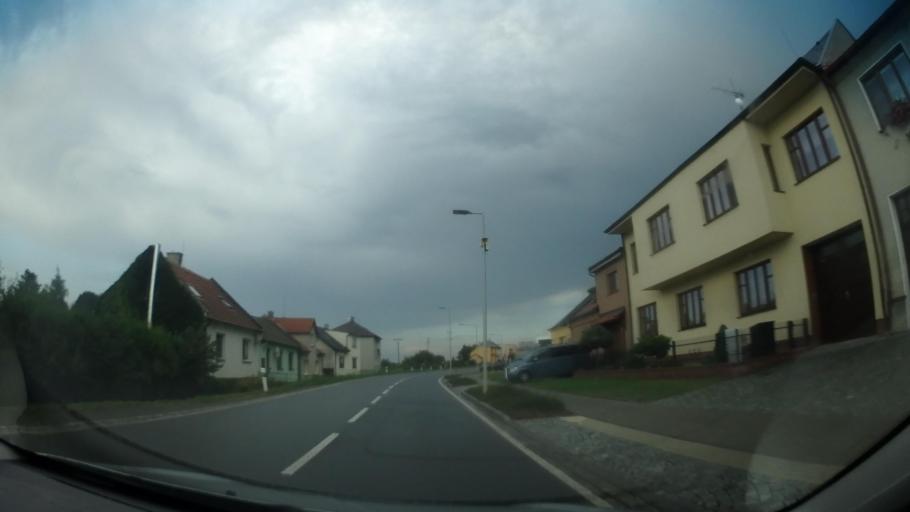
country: CZ
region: Olomoucky
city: Lostice
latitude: 49.7409
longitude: 16.9423
